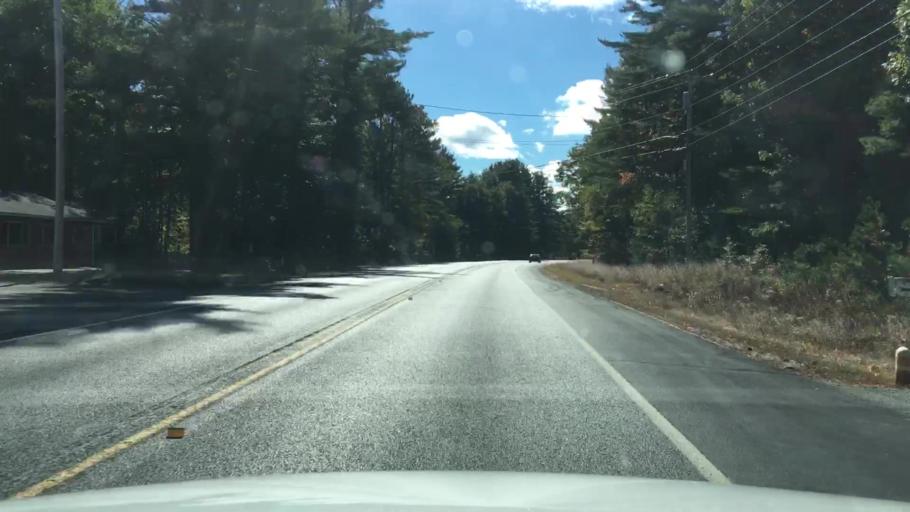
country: US
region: Maine
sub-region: York County
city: Alfred
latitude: 43.4527
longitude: -70.7233
